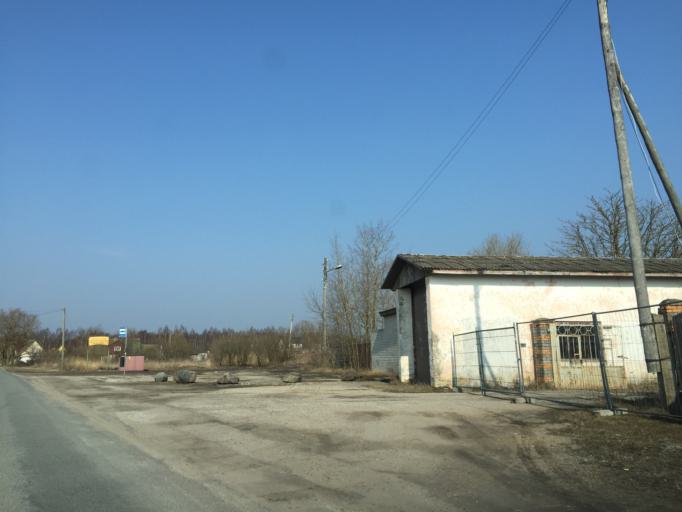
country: EE
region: Saare
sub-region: Kuressaare linn
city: Kuressaare
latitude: 58.2652
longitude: 22.4732
